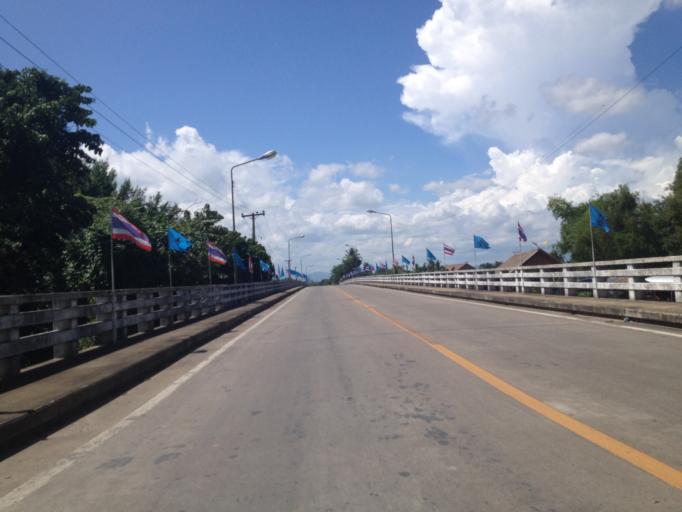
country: TH
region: Lamphun
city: Lamphun
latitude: 18.5983
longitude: 98.9672
